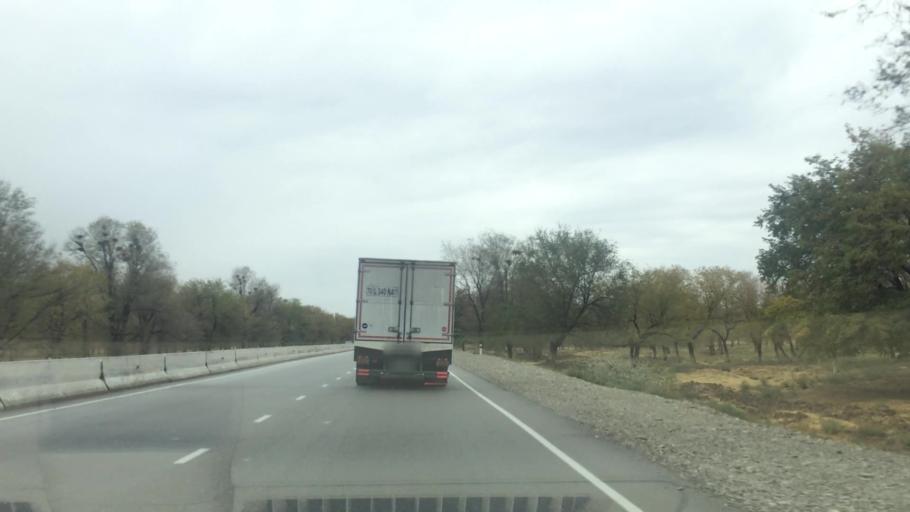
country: UZ
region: Samarqand
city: Bulung'ur
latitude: 39.8976
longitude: 67.4987
